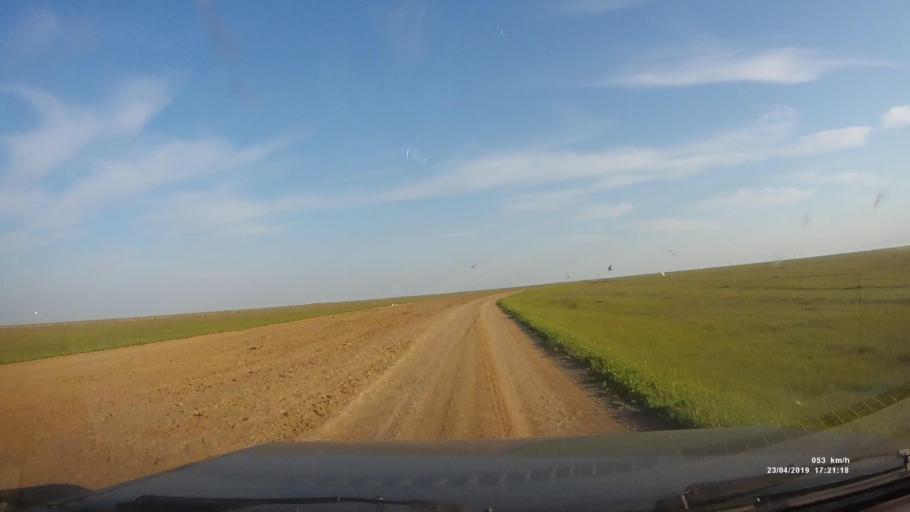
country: RU
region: Kalmykiya
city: Priyutnoye
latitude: 46.1772
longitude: 43.5048
